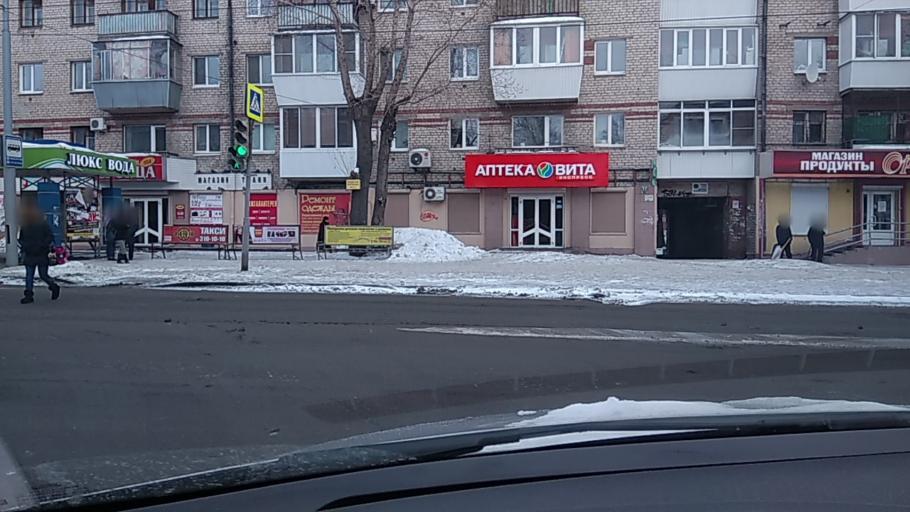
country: RU
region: Sverdlovsk
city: Yekaterinburg
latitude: 56.8050
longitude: 60.6254
